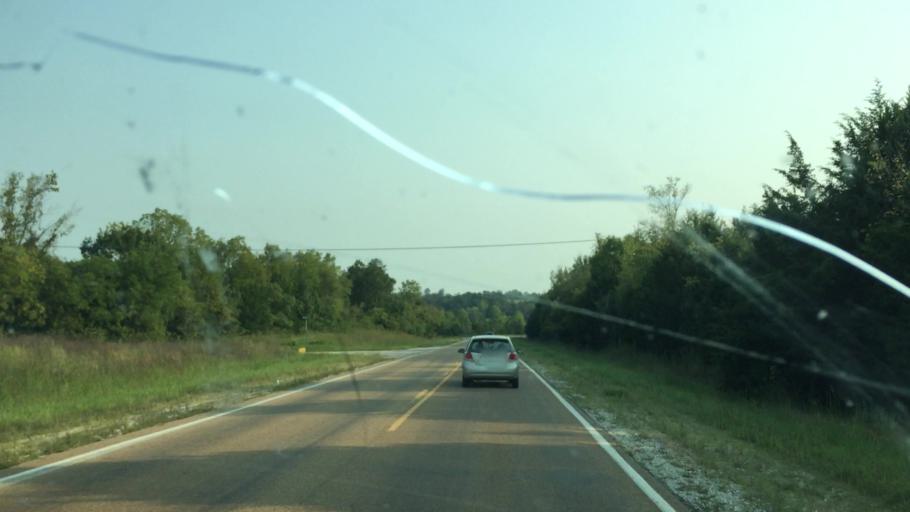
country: US
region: Missouri
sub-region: Pulaski County
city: Richland
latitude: 37.8256
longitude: -92.4054
